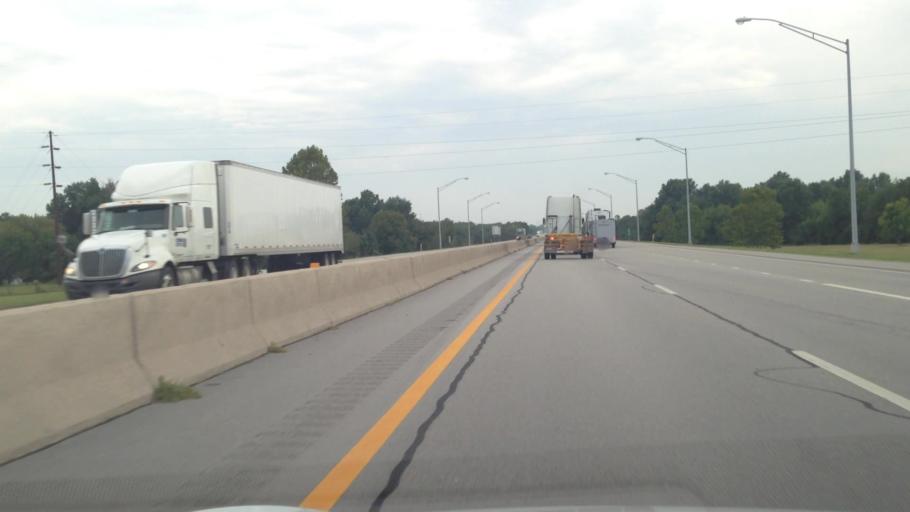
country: US
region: Oklahoma
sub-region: Ottawa County
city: Miami
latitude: 36.8630
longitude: -94.8510
